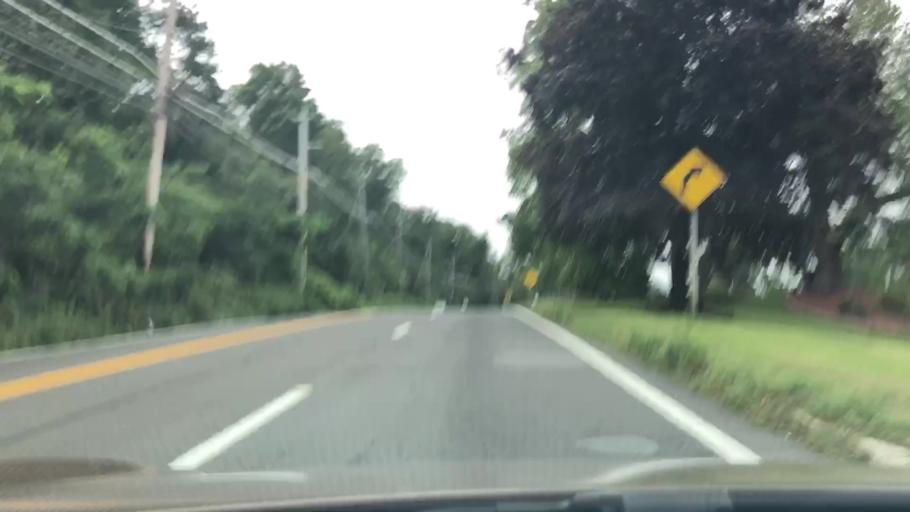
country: US
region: New York
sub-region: Westchester County
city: Sleepy Hollow
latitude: 41.1214
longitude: -73.8613
